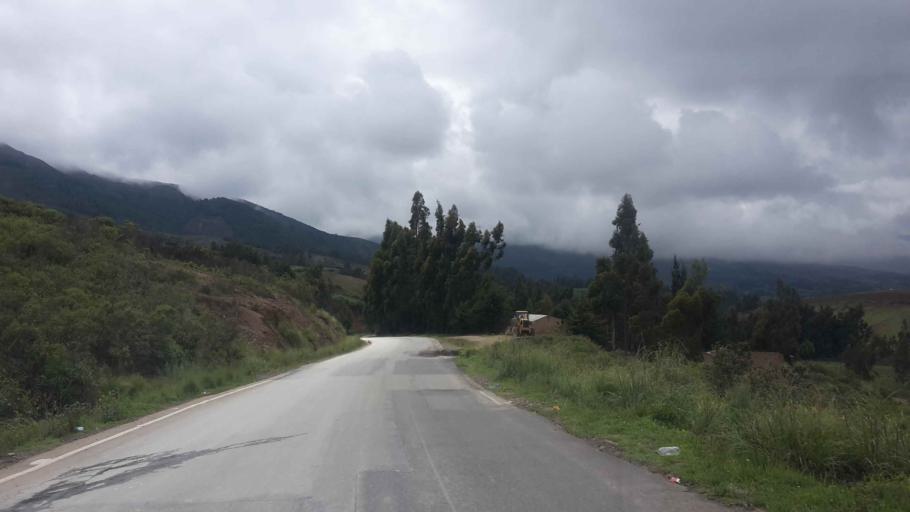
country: BO
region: Cochabamba
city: Totora
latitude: -17.5687
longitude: -65.3254
